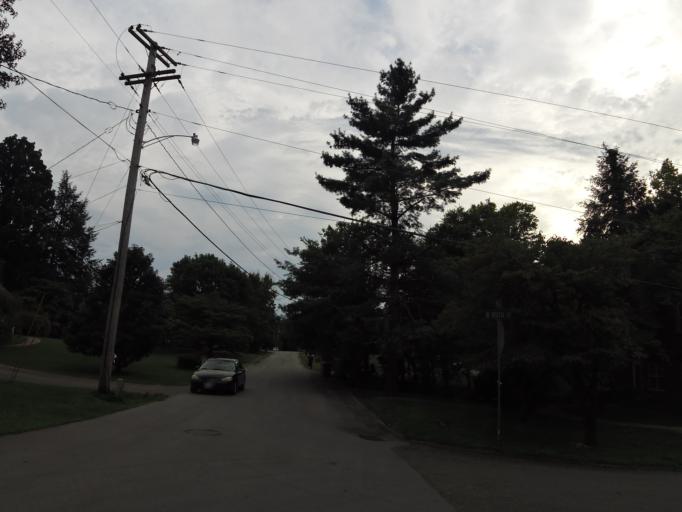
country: US
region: Tennessee
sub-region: Blount County
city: Maryville
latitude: 35.7474
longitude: -83.9833
